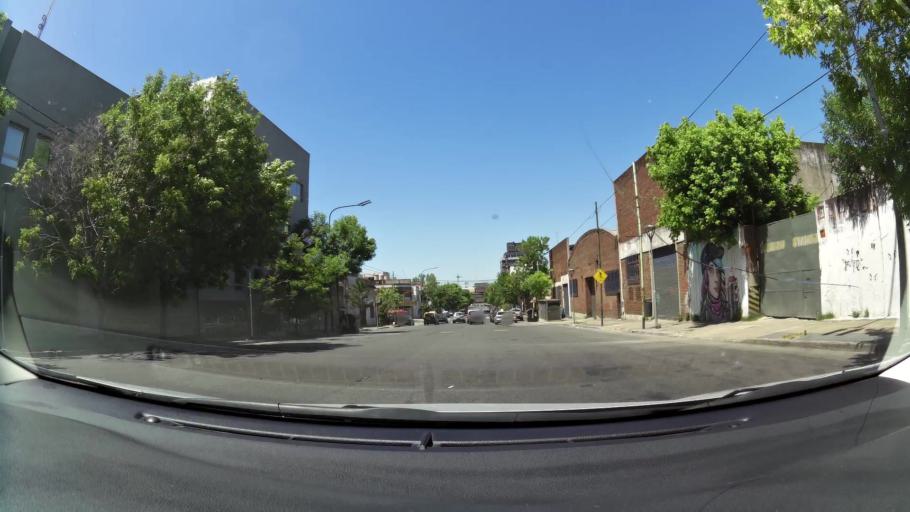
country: AR
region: Buenos Aires F.D.
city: Buenos Aires
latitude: -34.6375
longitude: -58.3982
